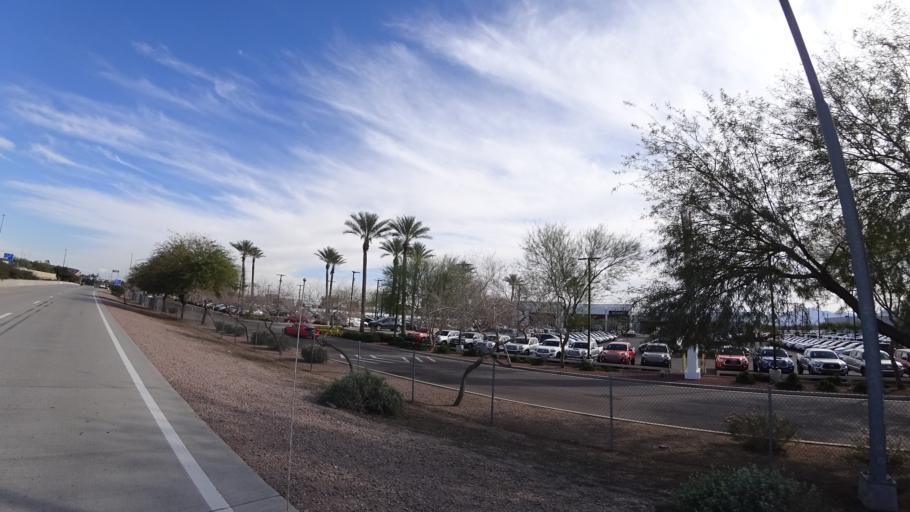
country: US
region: Arizona
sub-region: Maricopa County
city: Tolleson
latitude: 33.4610
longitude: -112.2768
